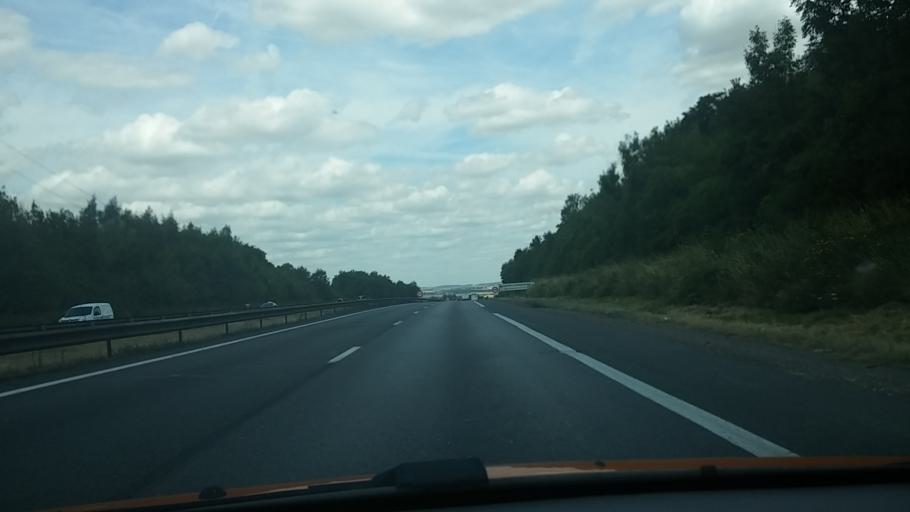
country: FR
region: Ile-de-France
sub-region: Departement de Seine-et-Marne
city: Le Pin
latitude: 48.9285
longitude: 2.6284
